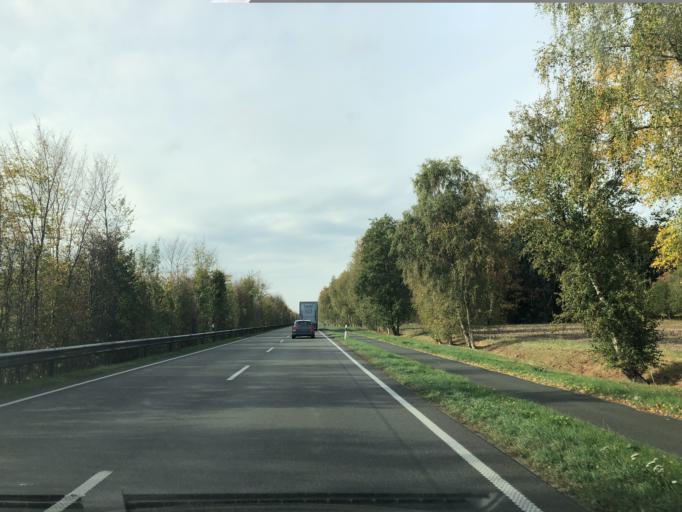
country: DE
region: Lower Saxony
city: Hilkenbrook
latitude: 53.0218
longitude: 7.7141
